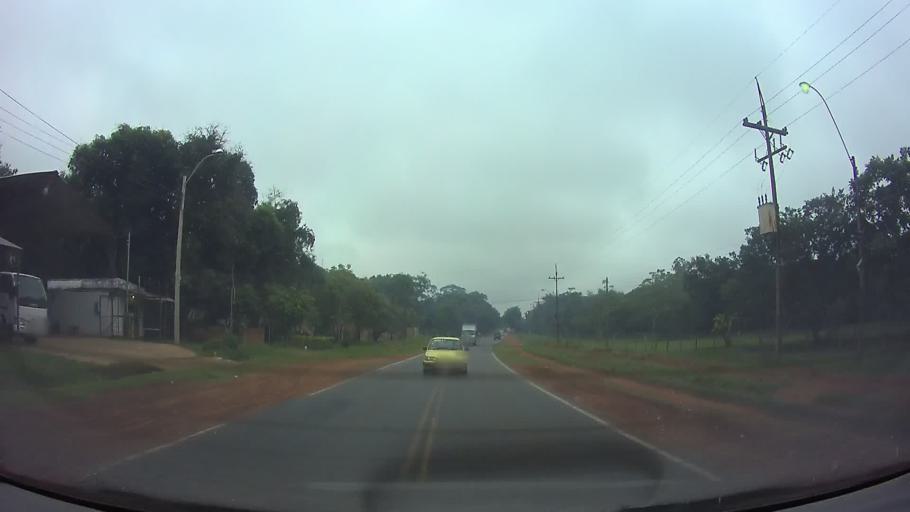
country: PY
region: Central
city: Itaugua
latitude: -25.4187
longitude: -57.3624
